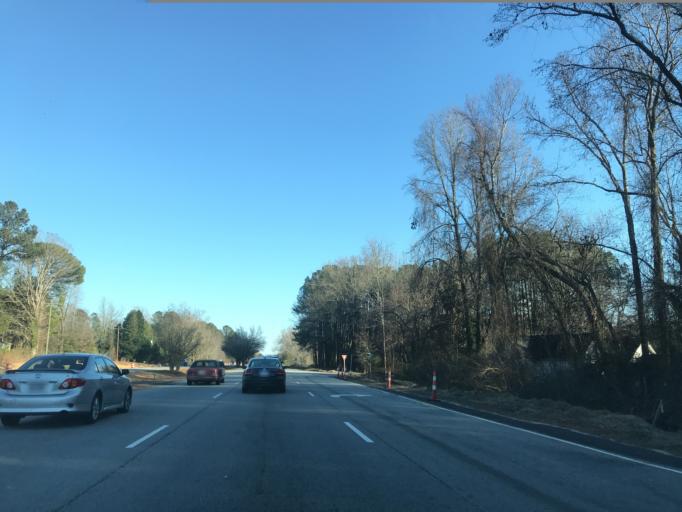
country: US
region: North Carolina
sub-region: Wake County
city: Garner
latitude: 35.7050
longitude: -78.6098
